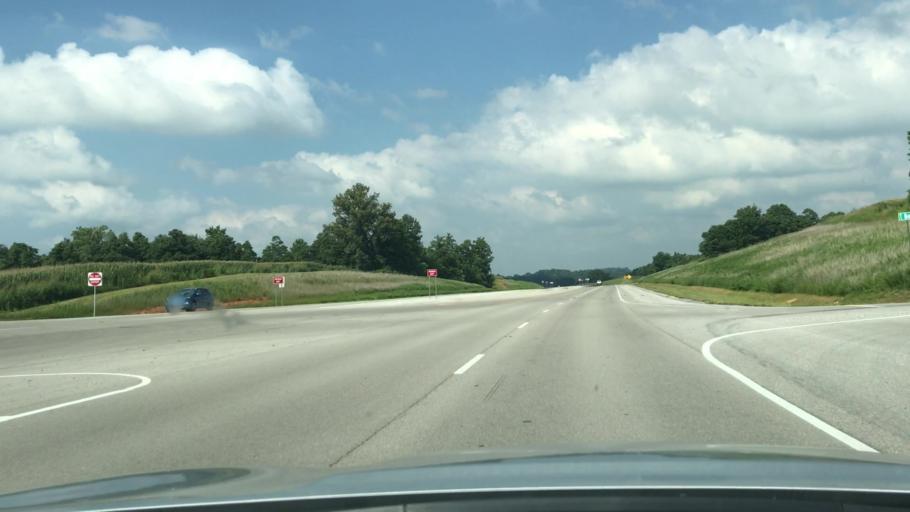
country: US
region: Kentucky
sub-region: Barren County
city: Glasgow
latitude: 36.9993
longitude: -85.9672
